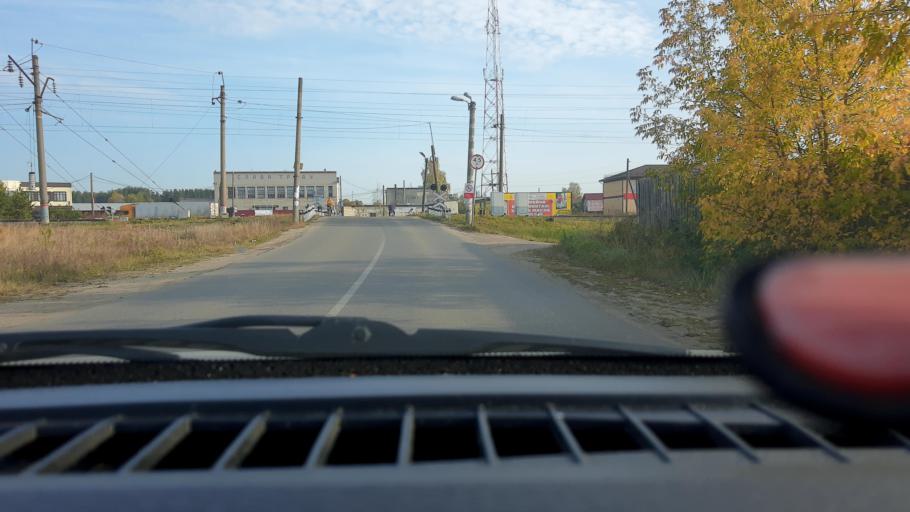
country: RU
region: Nizjnij Novgorod
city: Lukino
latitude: 56.4048
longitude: 43.7043
